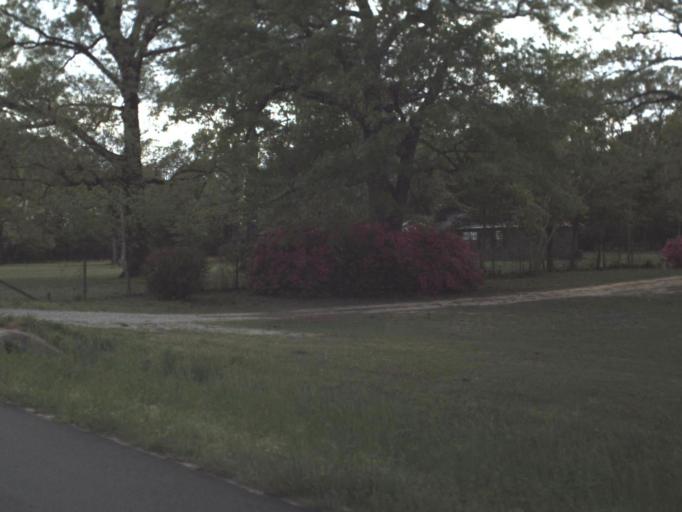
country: US
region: Florida
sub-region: Okaloosa County
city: Crestview
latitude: 30.8645
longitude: -86.5267
